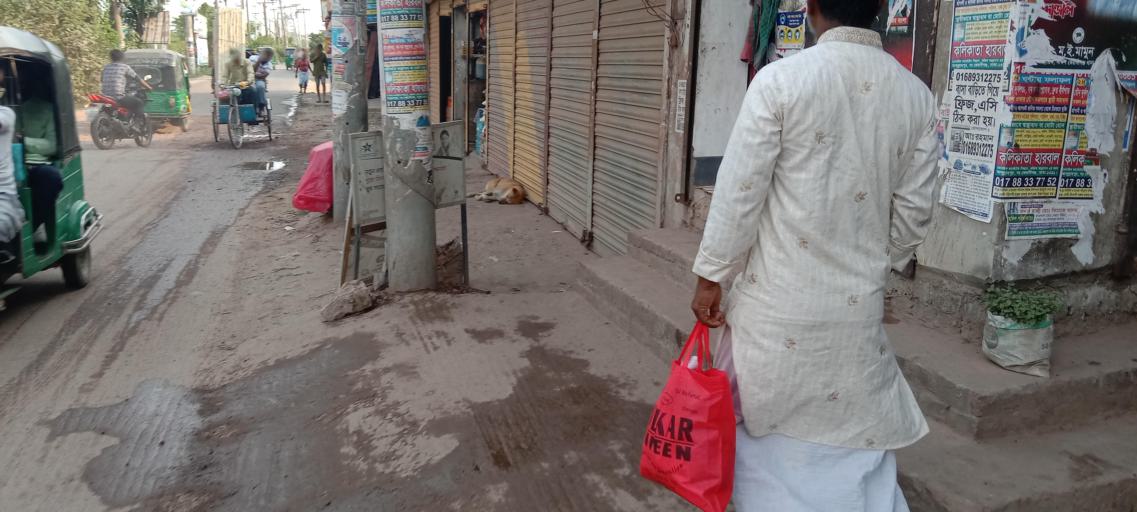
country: BD
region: Dhaka
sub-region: Dhaka
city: Dhaka
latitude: 23.6780
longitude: 90.4114
